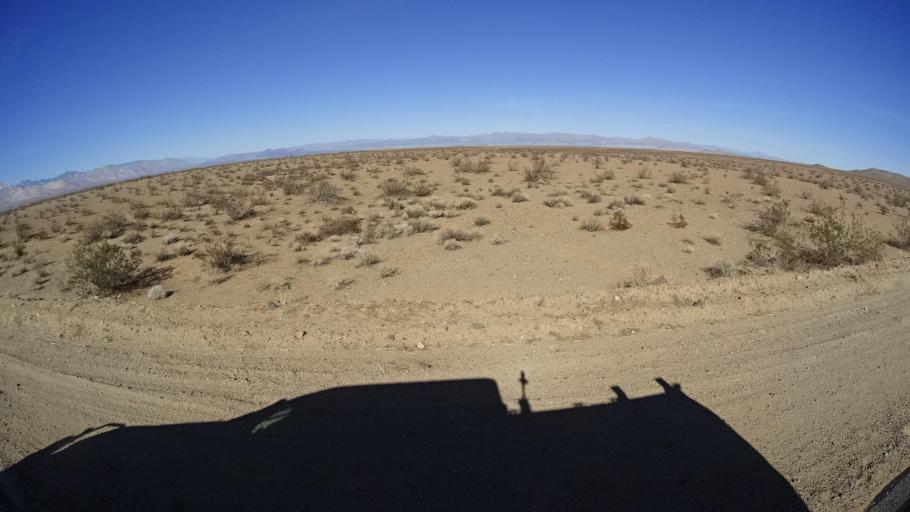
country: US
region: California
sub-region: Kern County
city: China Lake Acres
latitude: 35.5579
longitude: -117.7541
